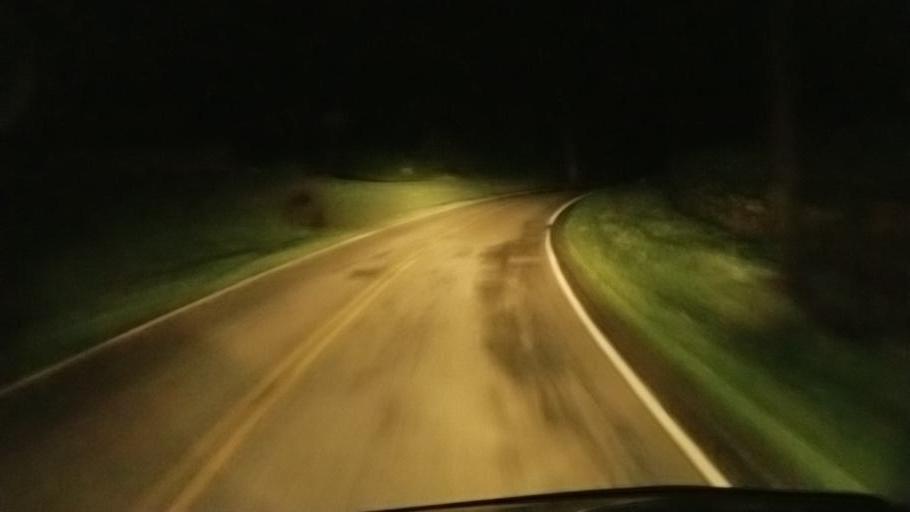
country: US
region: Ohio
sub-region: Coshocton County
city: Coshocton
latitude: 40.3429
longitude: -82.0134
